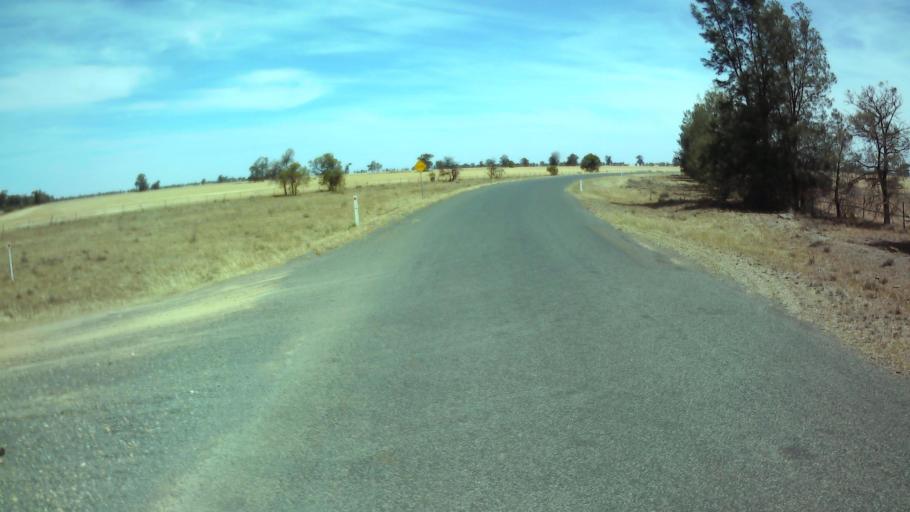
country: AU
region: New South Wales
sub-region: Weddin
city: Grenfell
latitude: -33.9113
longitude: 147.7654
